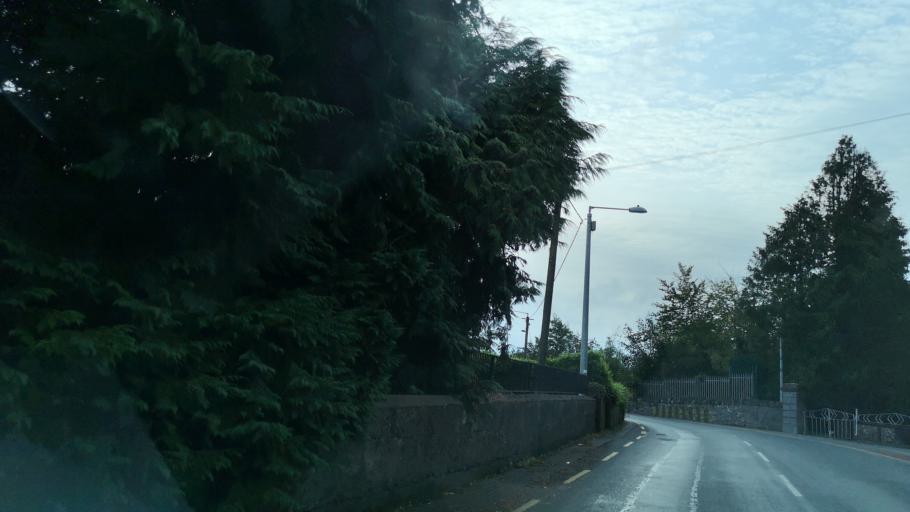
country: IE
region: Leinster
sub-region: An Iarmhi
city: Athlone
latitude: 53.4232
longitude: -7.9241
